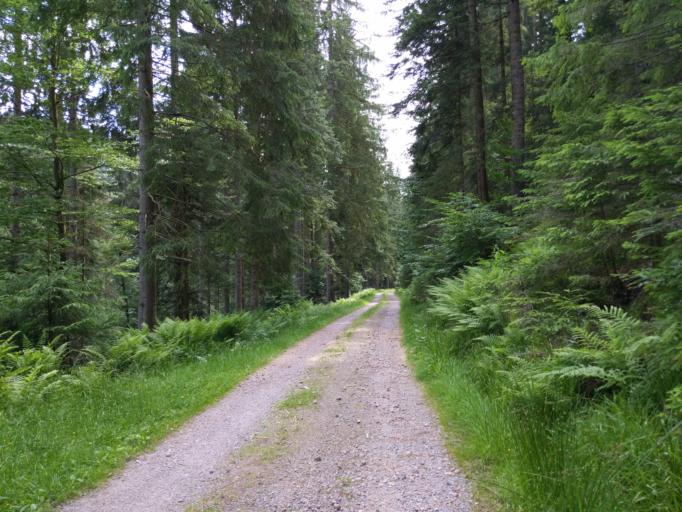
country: DE
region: Baden-Wuerttemberg
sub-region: Karlsruhe Region
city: Bad Rippoldsau-Schapbach
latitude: 48.4304
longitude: 8.3713
